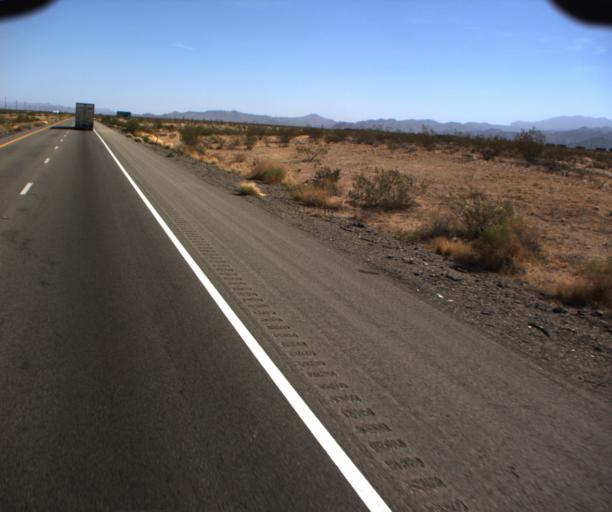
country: US
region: Arizona
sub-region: Mohave County
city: Kingman
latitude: 34.9299
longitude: -114.1494
